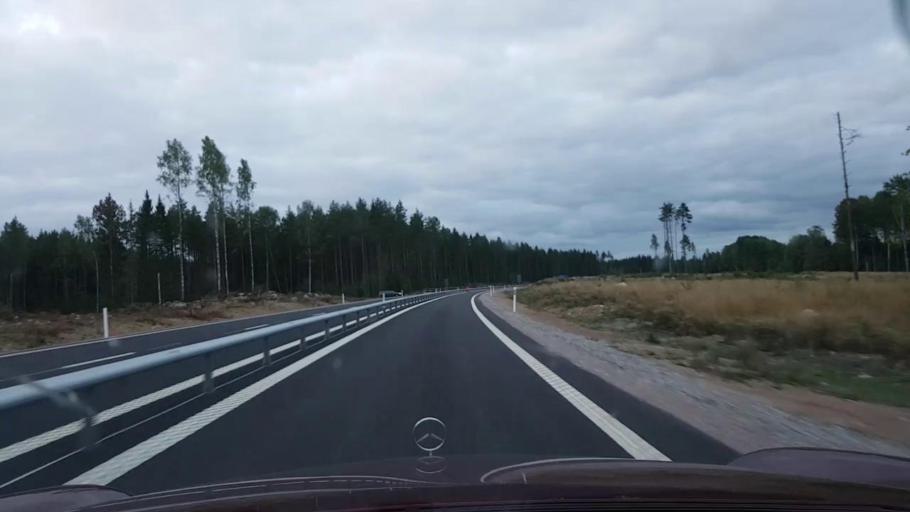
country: SE
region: Vaestmanland
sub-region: Hallstahammars Kommun
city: Hallstahammar
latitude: 59.6546
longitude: 16.2039
